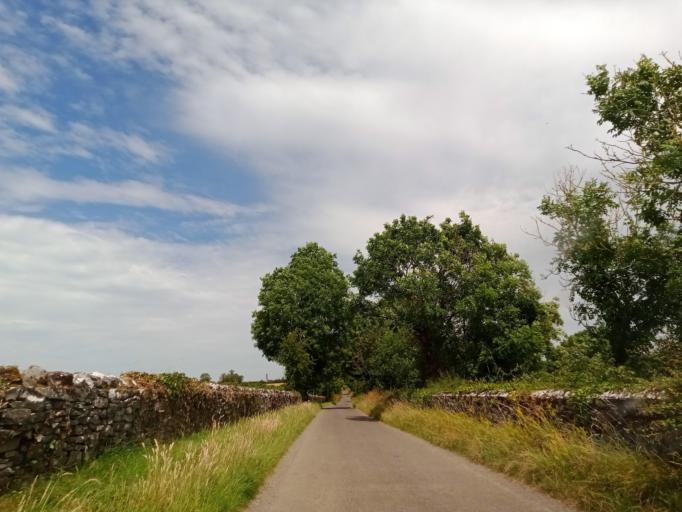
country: IE
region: Leinster
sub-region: Kilkenny
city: Thomastown
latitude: 52.5669
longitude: -7.1255
